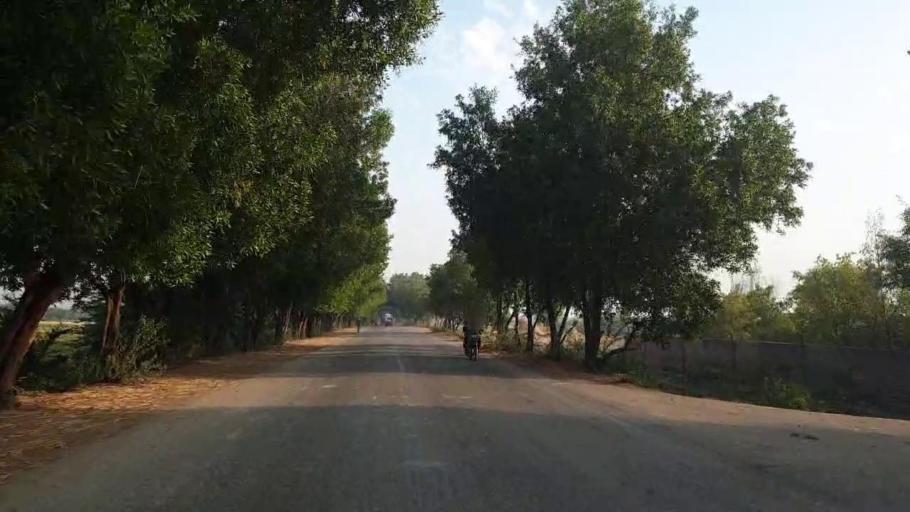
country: PK
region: Sindh
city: Tando Bago
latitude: 24.7707
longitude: 68.9586
